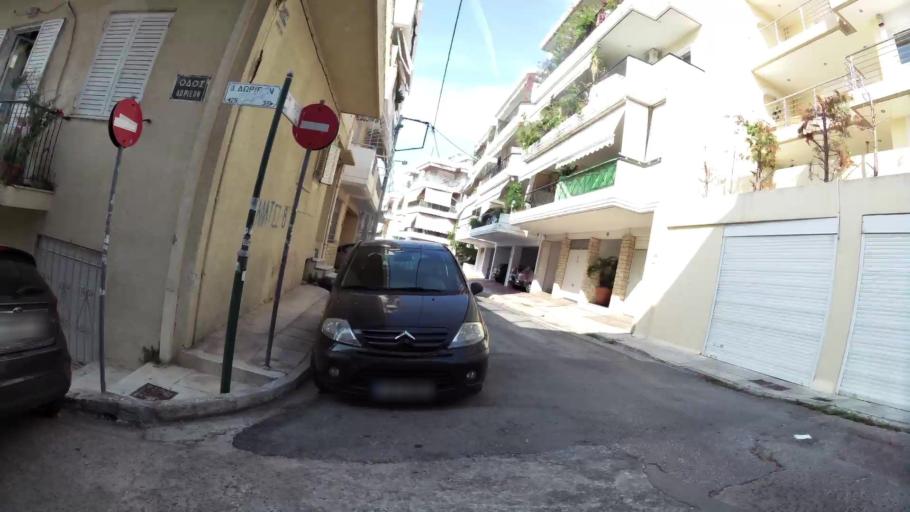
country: GR
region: Attica
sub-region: Nomarchia Athinas
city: Galatsi
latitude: 38.0169
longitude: 23.7479
